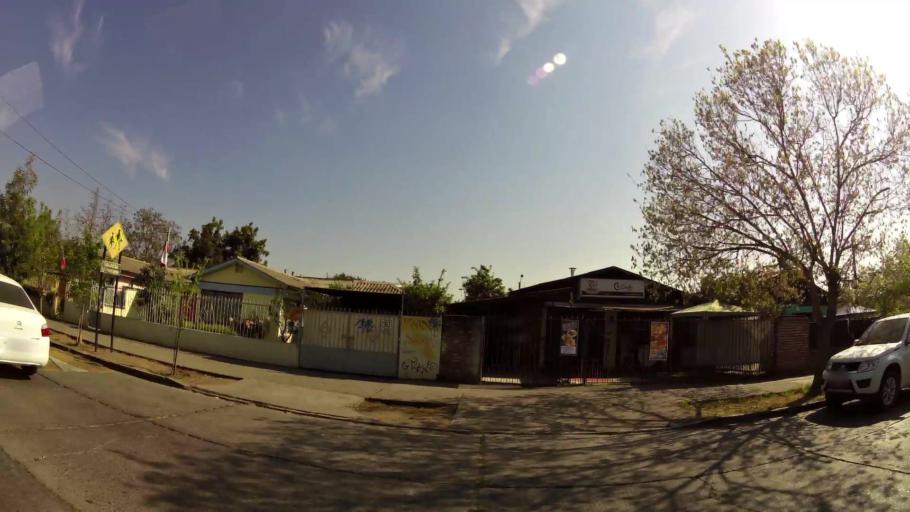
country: CL
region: Santiago Metropolitan
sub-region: Provincia de Santiago
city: La Pintana
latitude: -33.5577
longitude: -70.5908
